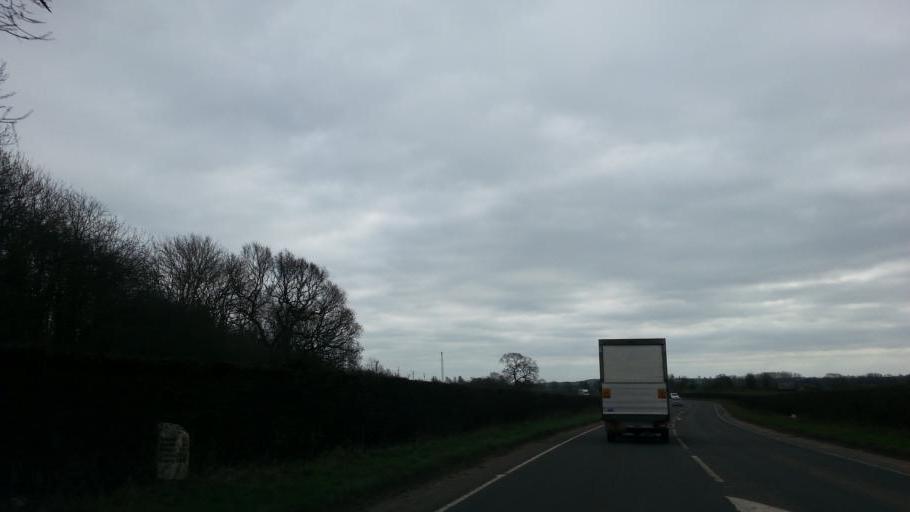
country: GB
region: England
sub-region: Staffordshire
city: Stone
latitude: 52.8826
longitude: -2.1162
